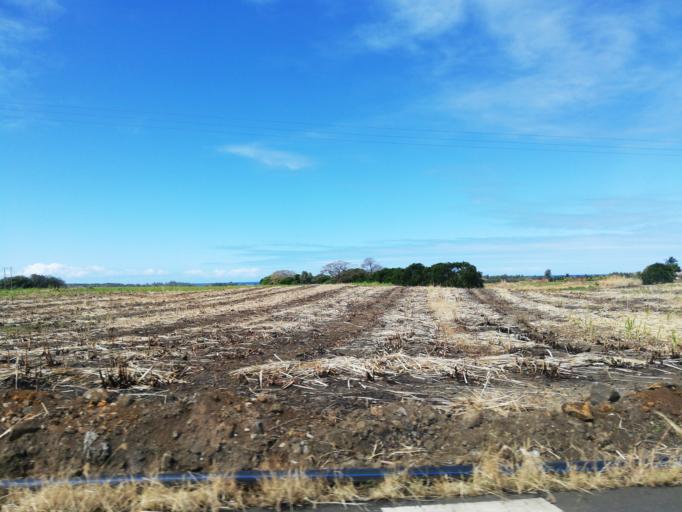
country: MU
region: Grand Port
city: Plaine Magnien
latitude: -20.4570
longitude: 57.6764
